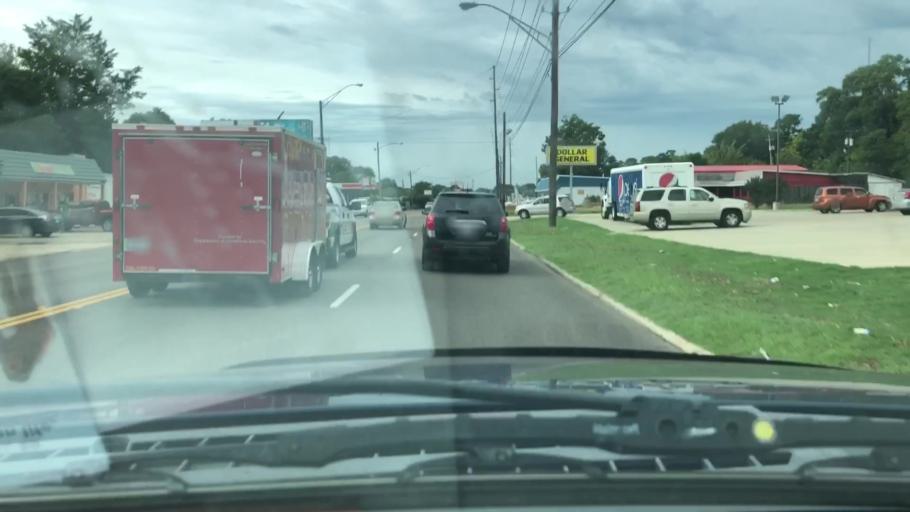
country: US
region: Texas
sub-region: Bowie County
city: Texarkana
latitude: 33.4350
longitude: -94.0694
